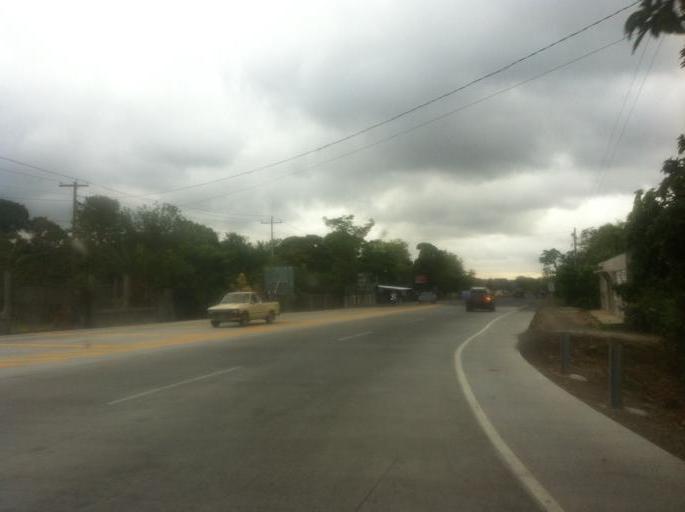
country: NI
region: Masaya
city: Nindiri
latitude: 11.9975
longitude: -86.1084
